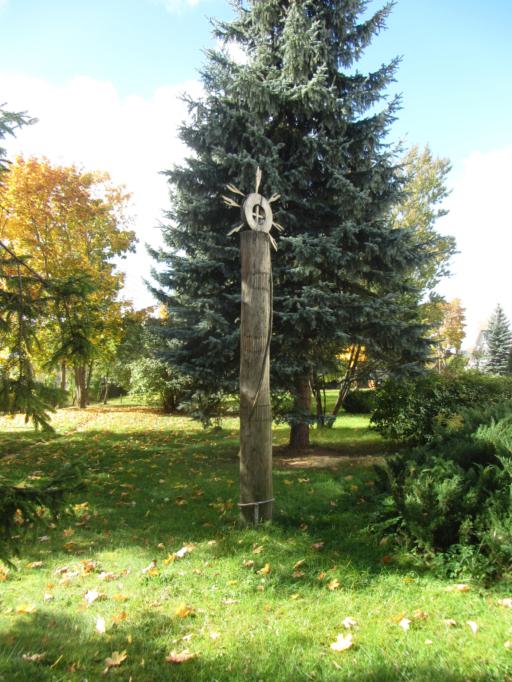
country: LT
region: Utenos apskritis
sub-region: Utena
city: Utena
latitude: 55.5046
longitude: 25.6134
